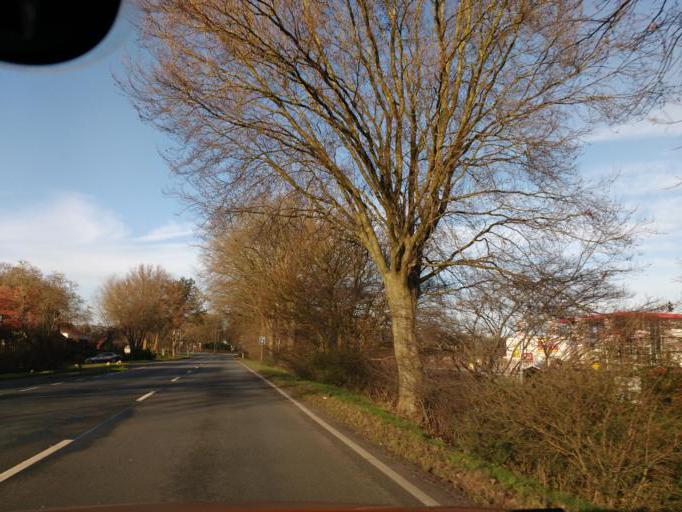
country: DE
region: Lower Saxony
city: Oldenburg
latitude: 53.1055
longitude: 8.2778
